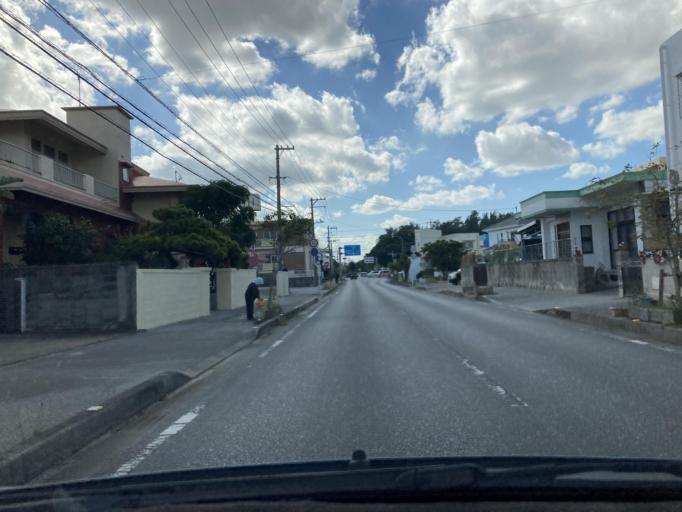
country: JP
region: Okinawa
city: Gushikawa
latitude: 26.3414
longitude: 127.8457
